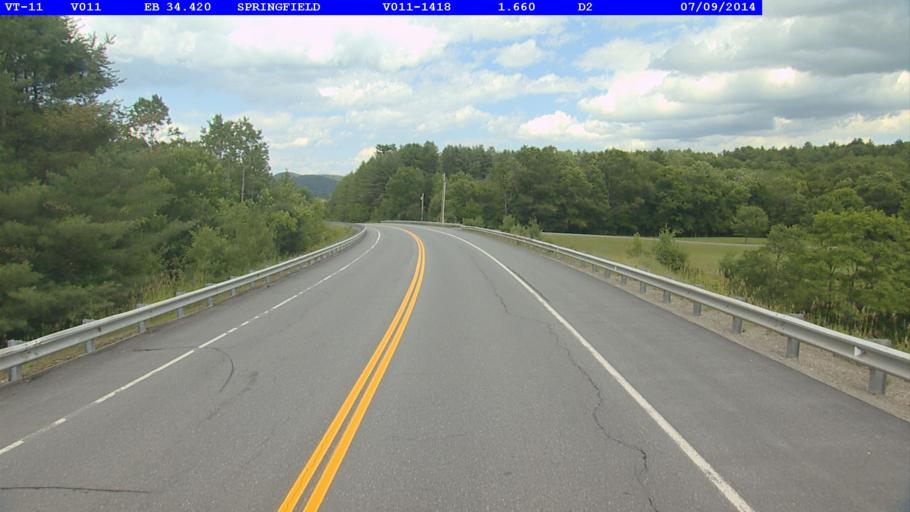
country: US
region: Vermont
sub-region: Windsor County
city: Springfield
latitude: 43.2900
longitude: -72.5231
